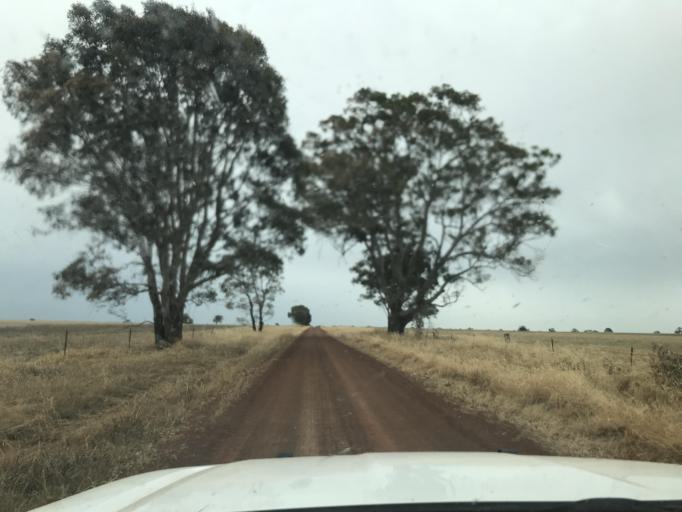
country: AU
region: Victoria
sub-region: Horsham
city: Horsham
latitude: -37.0643
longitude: 141.6482
